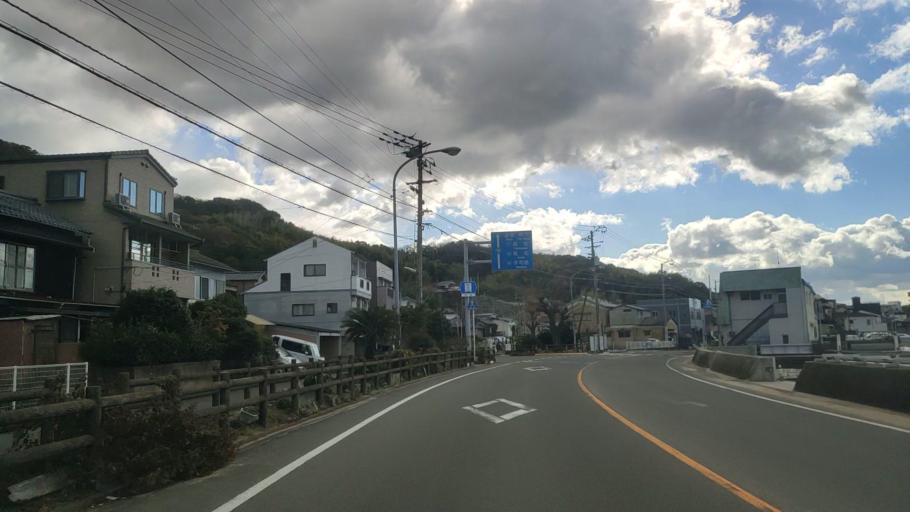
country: JP
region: Ehime
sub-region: Shikoku-chuo Shi
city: Matsuyama
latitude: 33.8851
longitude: 132.7013
